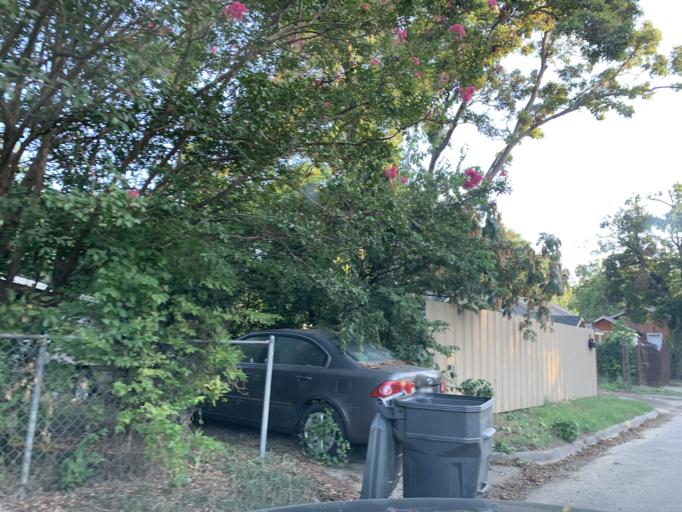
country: US
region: Texas
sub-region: Dallas County
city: Dallas
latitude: 32.7546
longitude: -96.7606
